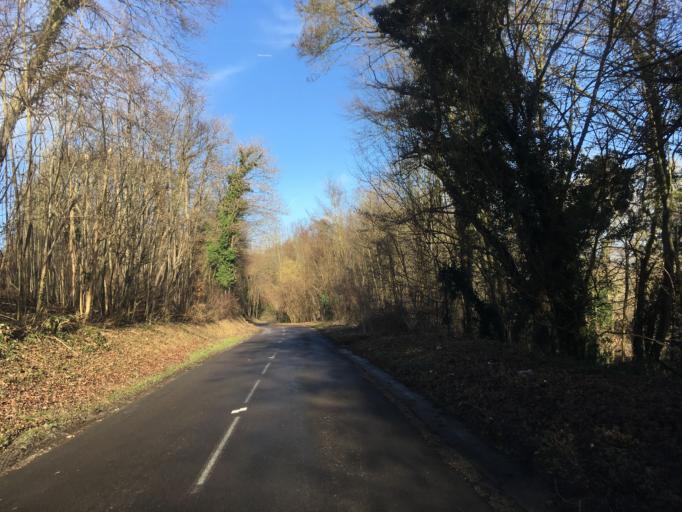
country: FR
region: Haute-Normandie
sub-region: Departement de l'Eure
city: Saint-Just
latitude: 49.1002
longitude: 1.4335
